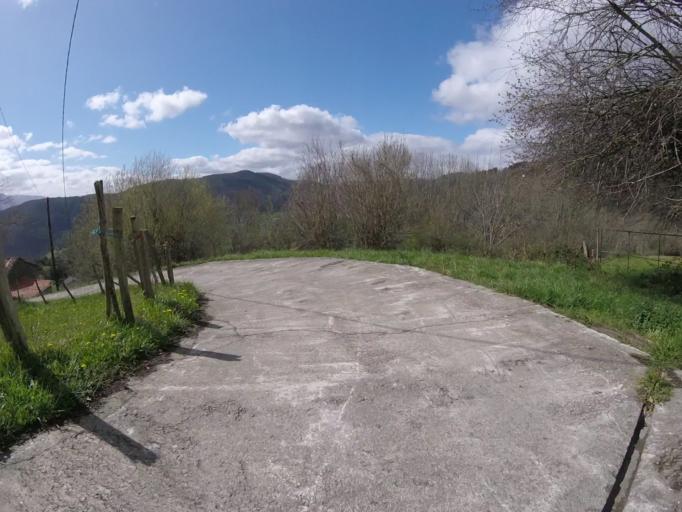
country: ES
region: Basque Country
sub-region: Provincia de Guipuzcoa
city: Albiztur
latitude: 43.1386
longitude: -2.1272
